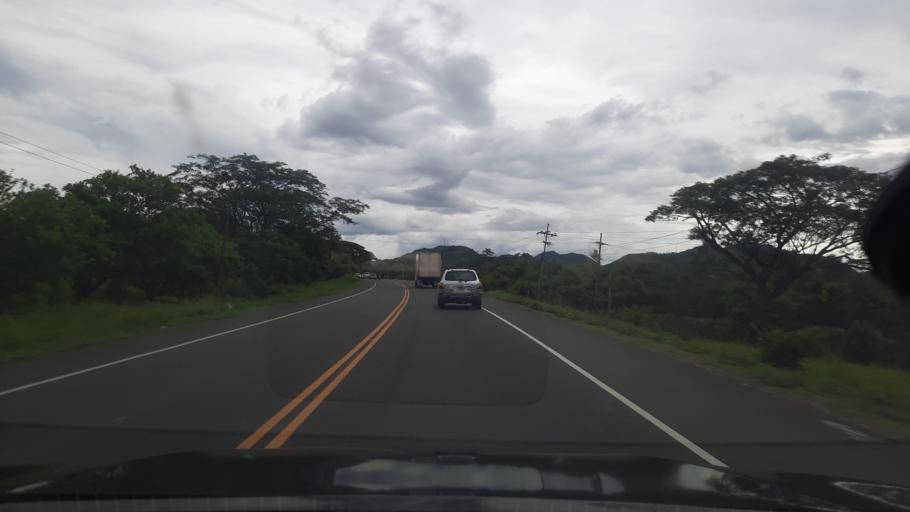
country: HN
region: Choluteca
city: Marcovia
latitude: 13.3734
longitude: -87.3001
